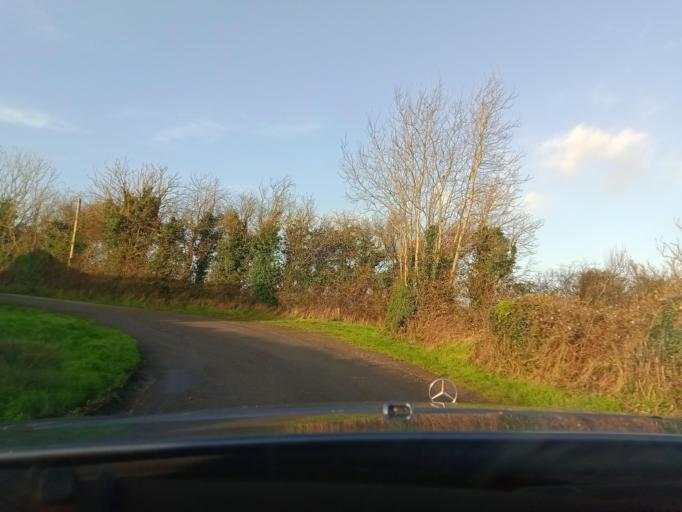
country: IE
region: Leinster
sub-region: Kilkenny
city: Callan
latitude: 52.4787
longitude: -7.4667
